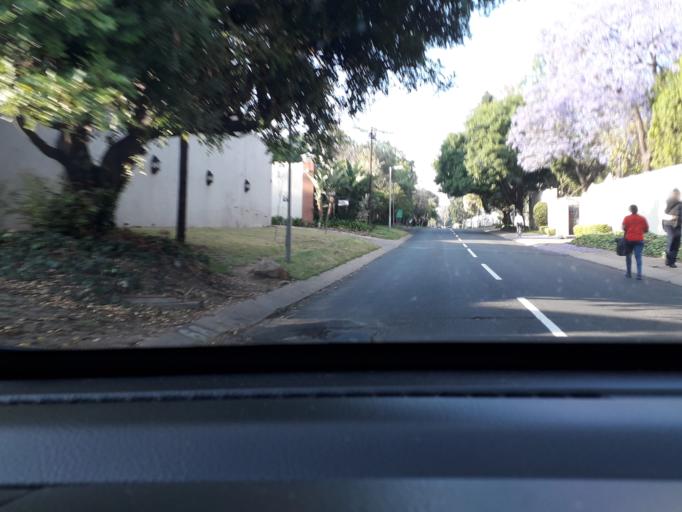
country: ZA
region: Gauteng
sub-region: City of Johannesburg Metropolitan Municipality
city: Modderfontein
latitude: -26.0831
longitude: 28.0575
